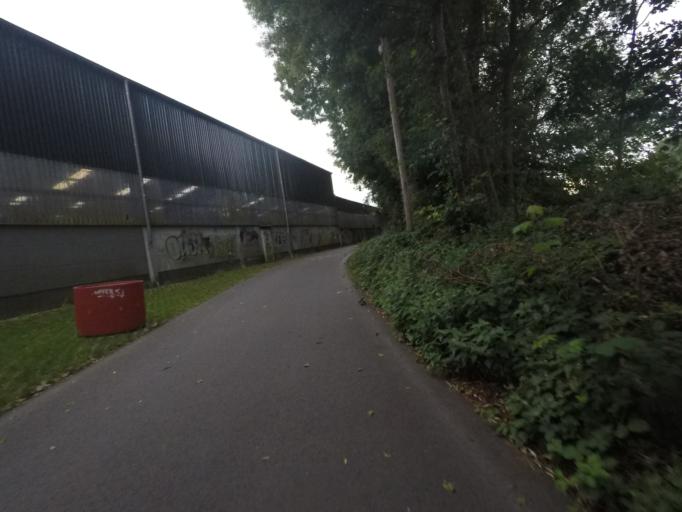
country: DE
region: North Rhine-Westphalia
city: Bad Oeynhausen
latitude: 52.2114
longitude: 8.8095
